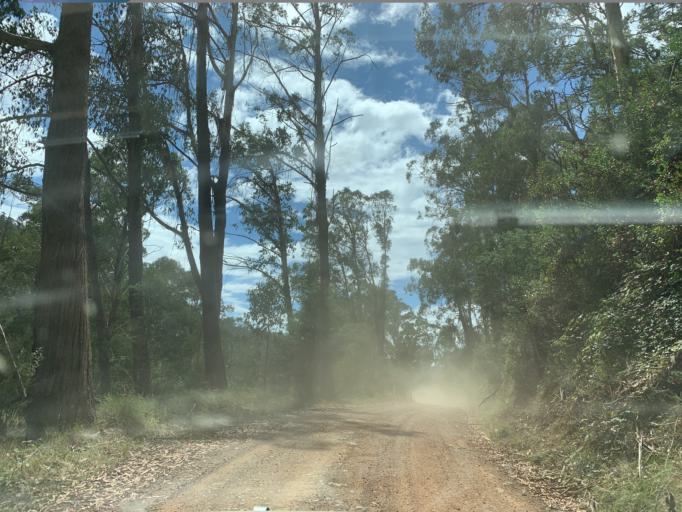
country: AU
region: Victoria
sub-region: Mansfield
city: Mansfield
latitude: -37.1049
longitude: 146.5015
